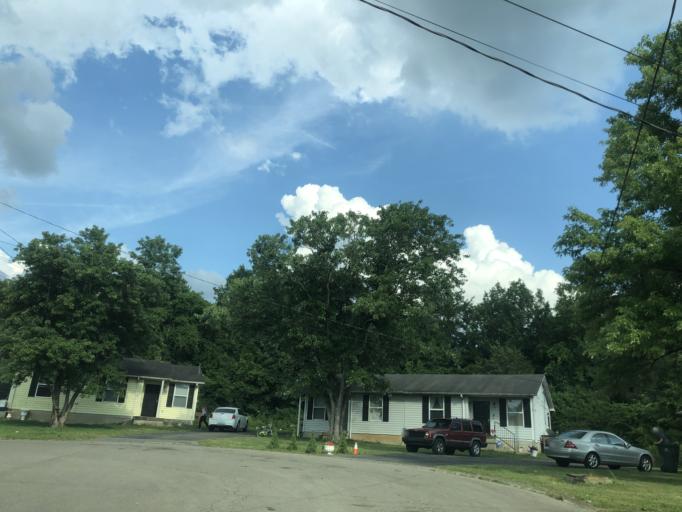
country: US
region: Tennessee
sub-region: Davidson County
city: Nashville
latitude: 36.2300
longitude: -86.7954
